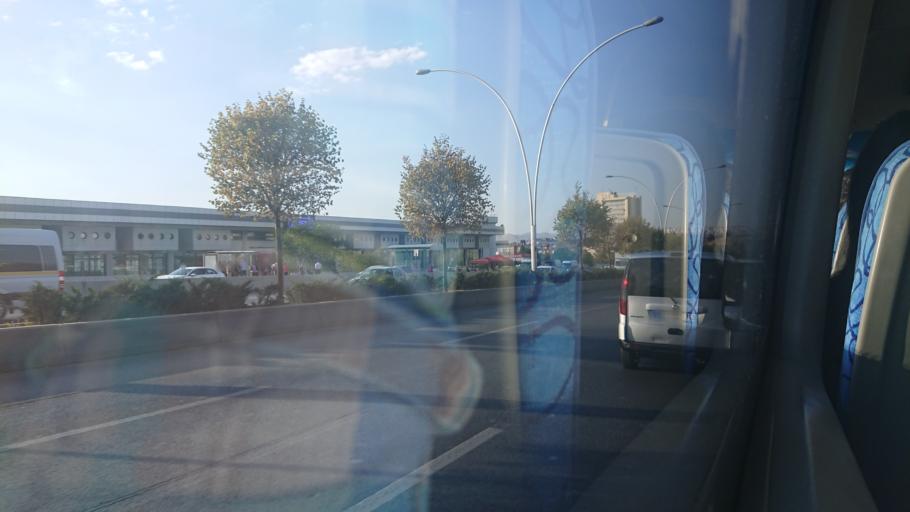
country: TR
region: Ankara
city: Ankara
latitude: 39.9174
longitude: 32.8143
